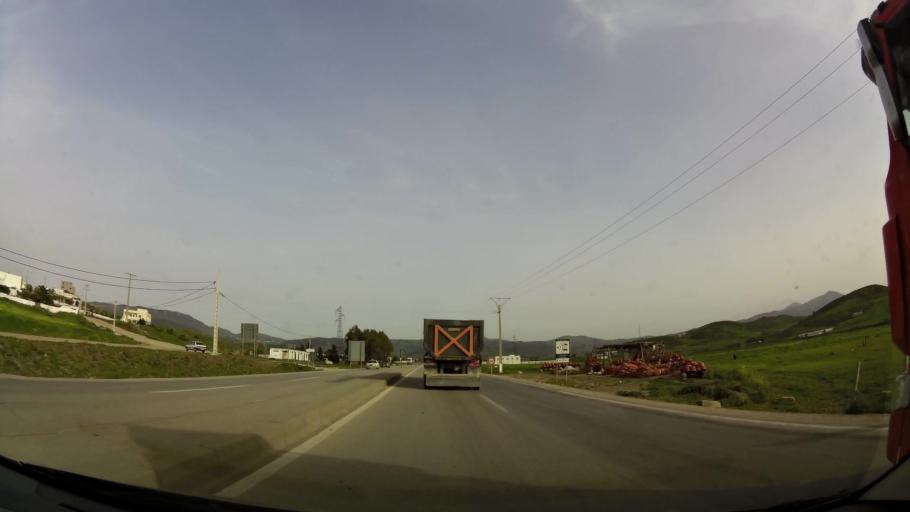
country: MA
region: Tanger-Tetouan
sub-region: Tanger-Assilah
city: Dar Chaoui
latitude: 35.5827
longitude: -5.6386
